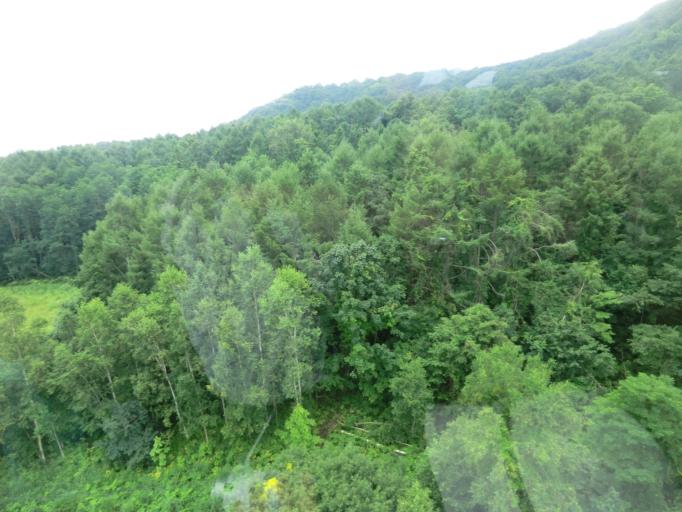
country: JP
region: Hokkaido
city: Date
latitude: 42.5389
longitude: 140.8574
